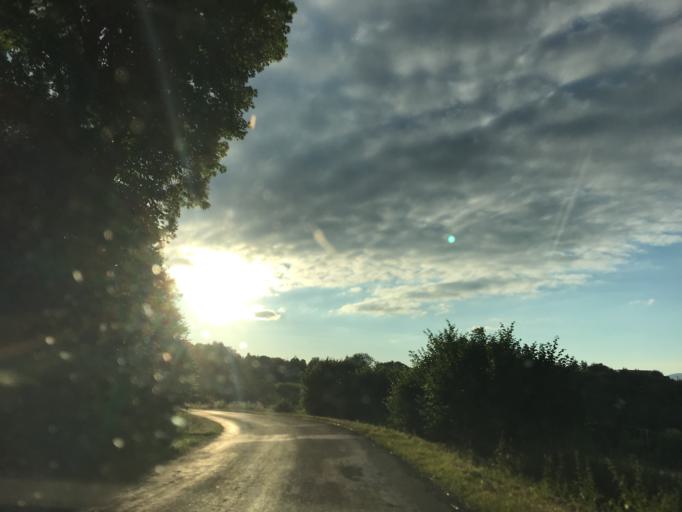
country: FR
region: Rhone-Alpes
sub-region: Departement de la Loire
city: Noiretable
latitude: 45.7733
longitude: 3.8159
